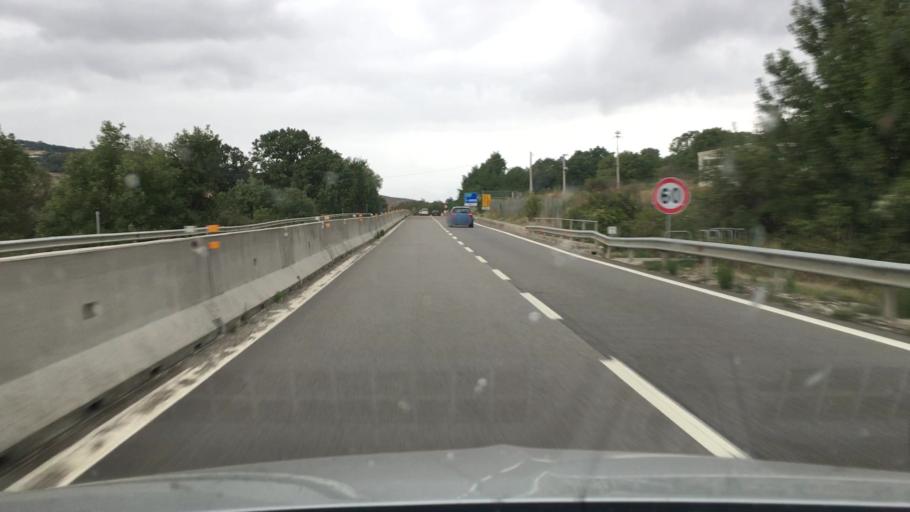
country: IT
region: Basilicate
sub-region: Provincia di Potenza
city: Vaglio Basilicata
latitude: 40.6510
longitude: 15.9108
